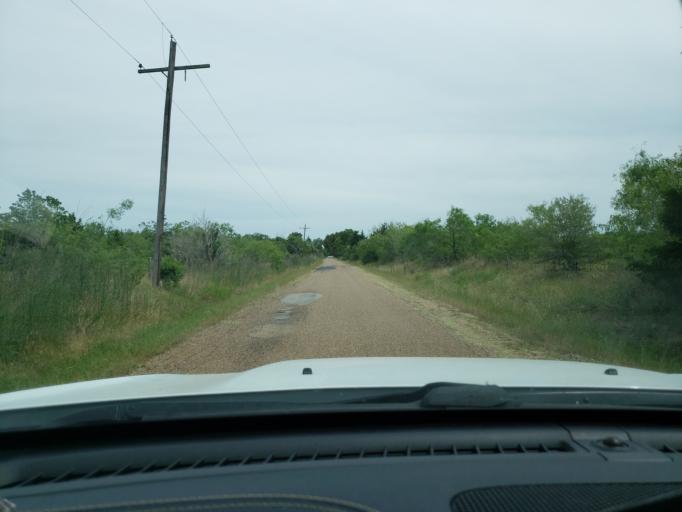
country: US
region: Texas
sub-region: Burleson County
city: Somerville
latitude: 30.3541
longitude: -96.5466
